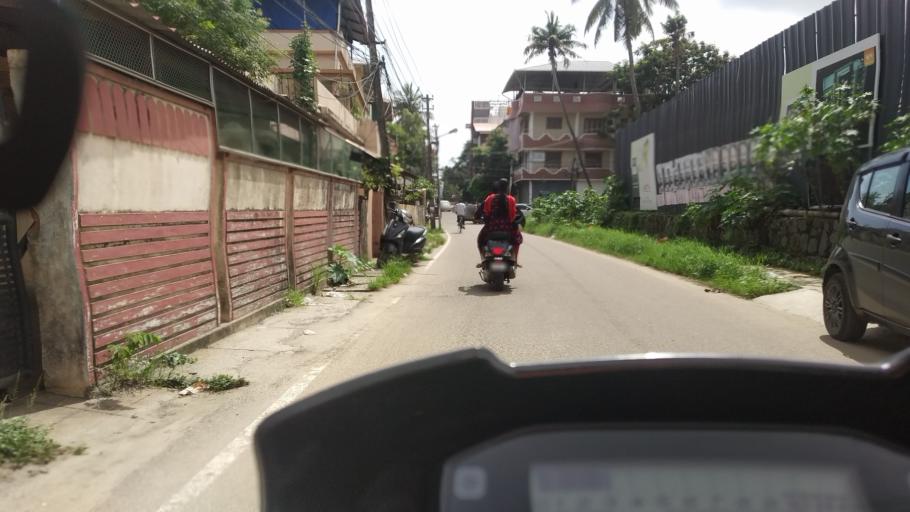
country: IN
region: Kerala
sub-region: Ernakulam
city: Cochin
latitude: 9.9849
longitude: 76.2927
